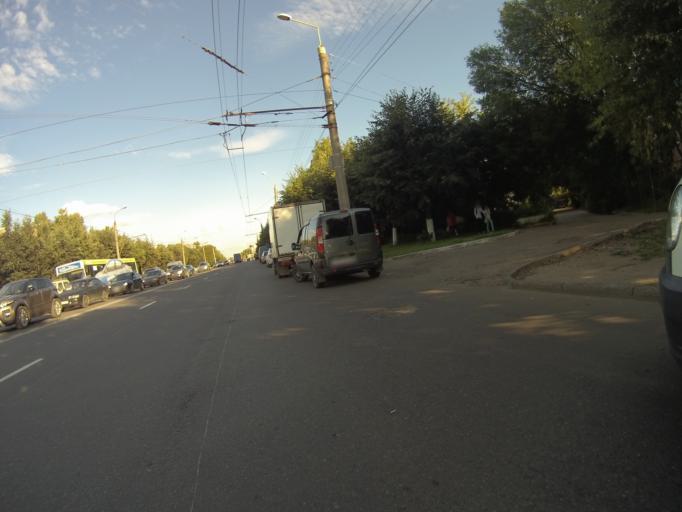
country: RU
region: Vladimir
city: Vladimir
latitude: 56.1487
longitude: 40.3763
